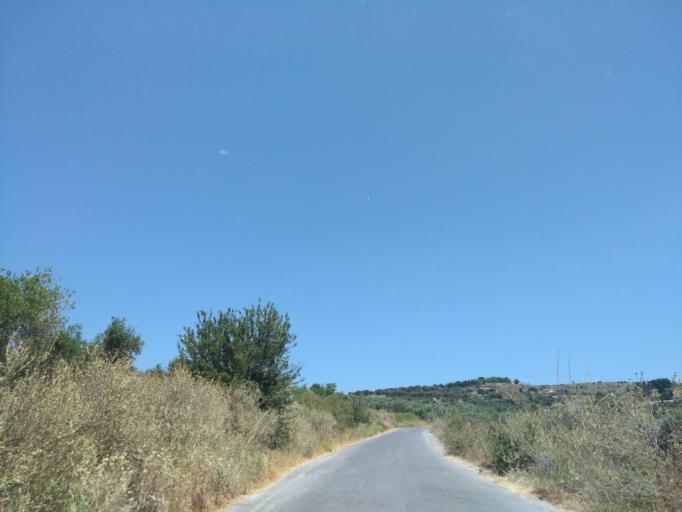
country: GR
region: Crete
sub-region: Nomos Chanias
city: Georgioupolis
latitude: 35.3256
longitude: 24.3253
